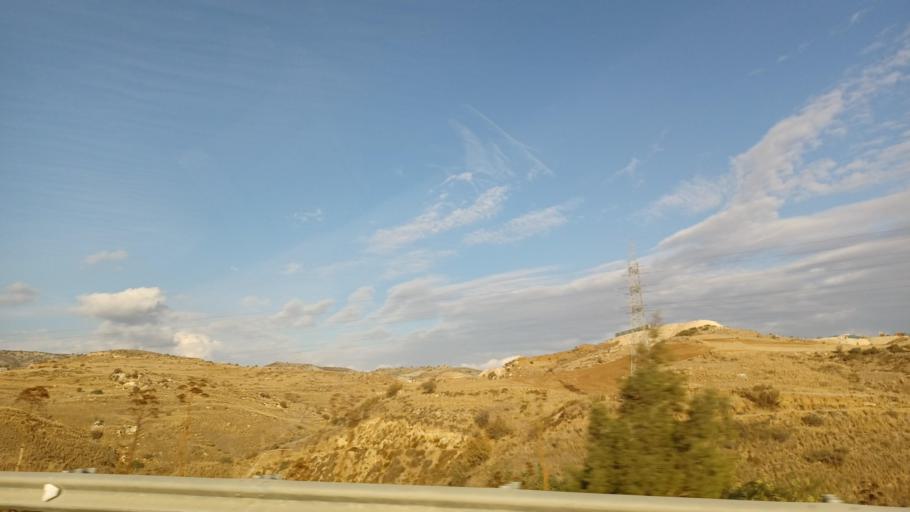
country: CY
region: Pafos
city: Mesogi
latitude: 34.7598
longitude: 32.4914
